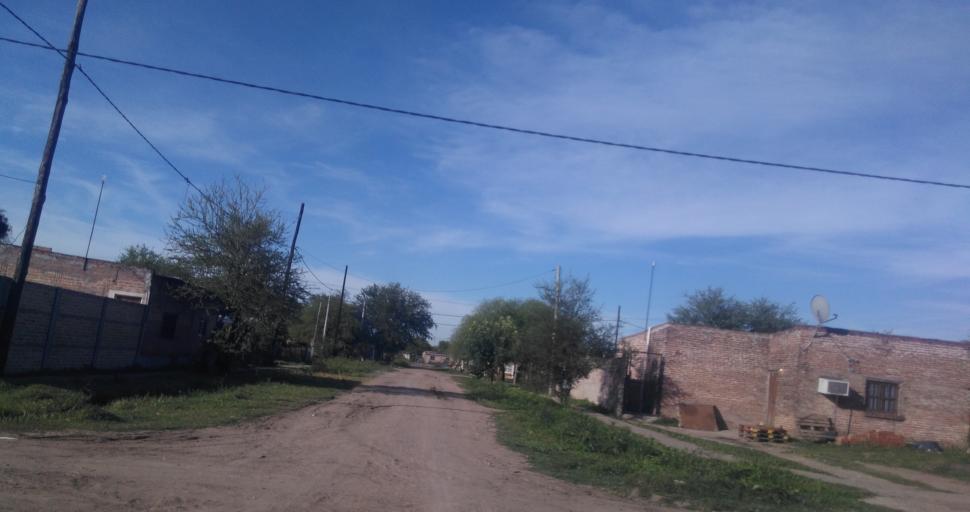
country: AR
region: Chaco
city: Fontana
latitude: -27.4232
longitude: -59.0392
